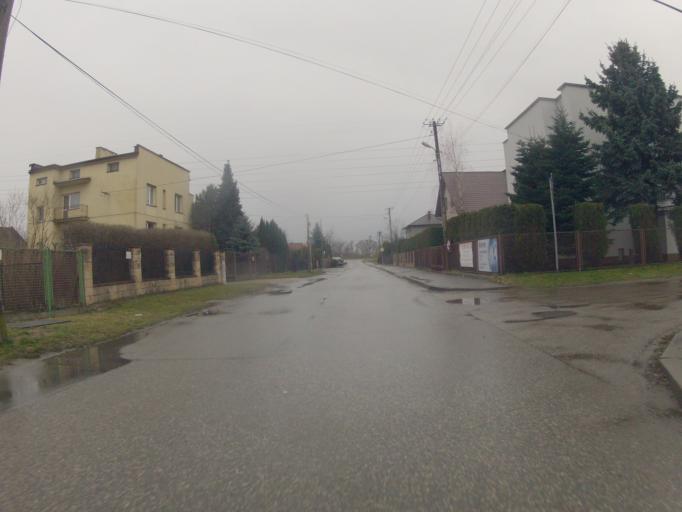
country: PL
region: Lesser Poland Voivodeship
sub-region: Powiat wielicki
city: Kokotow
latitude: 50.0553
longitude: 20.0456
